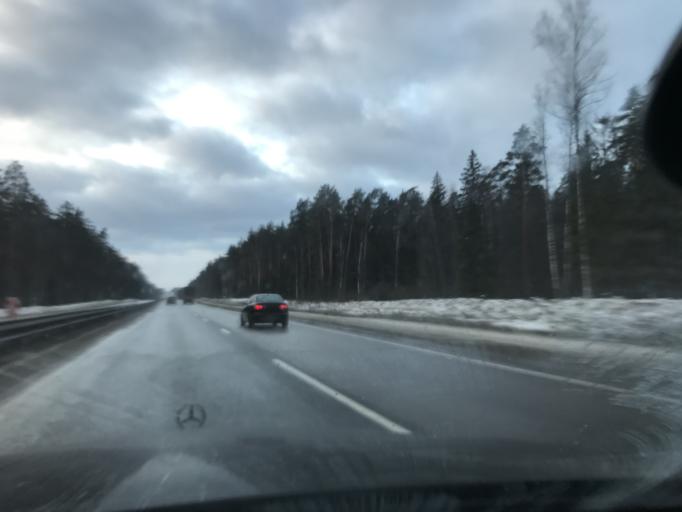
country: RU
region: Vladimir
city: Kameshkovo
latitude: 56.1988
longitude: 41.0425
